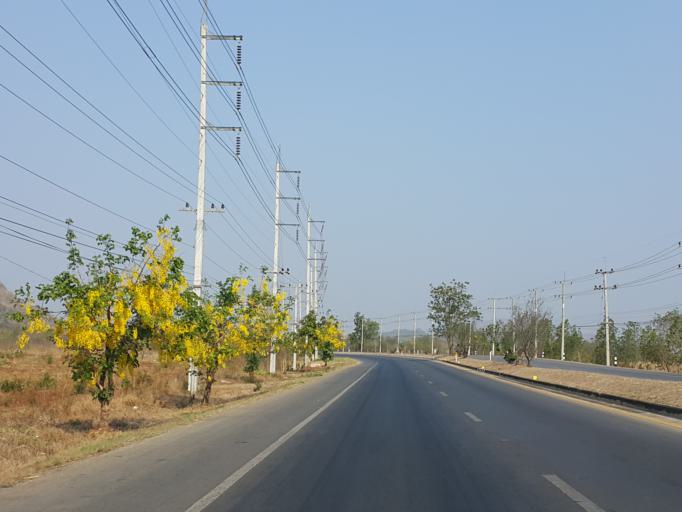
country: TH
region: Kanchanaburi
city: Kanchanaburi
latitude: 14.0682
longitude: 99.4078
